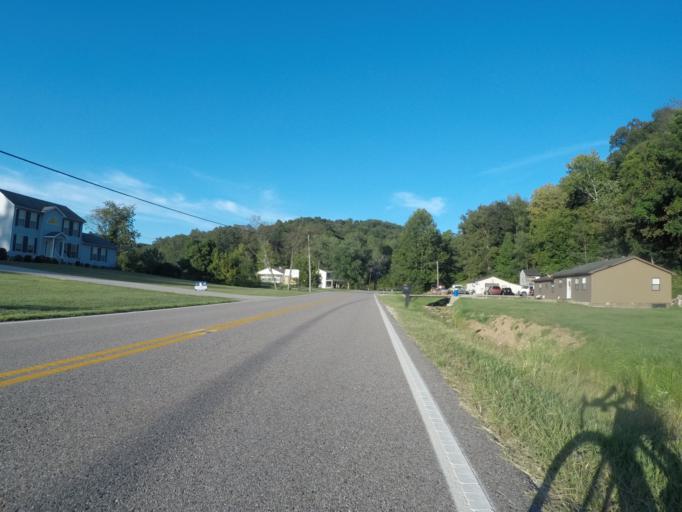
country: US
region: Ohio
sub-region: Lawrence County
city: Coal Grove
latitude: 38.5731
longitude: -82.5470
